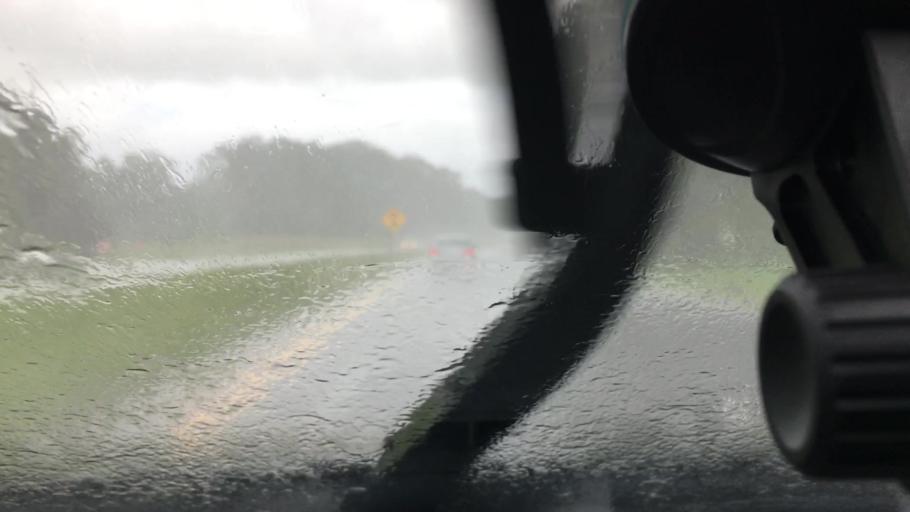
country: US
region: North Carolina
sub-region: Cleveland County
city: White Plains
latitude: 35.2619
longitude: -81.4656
